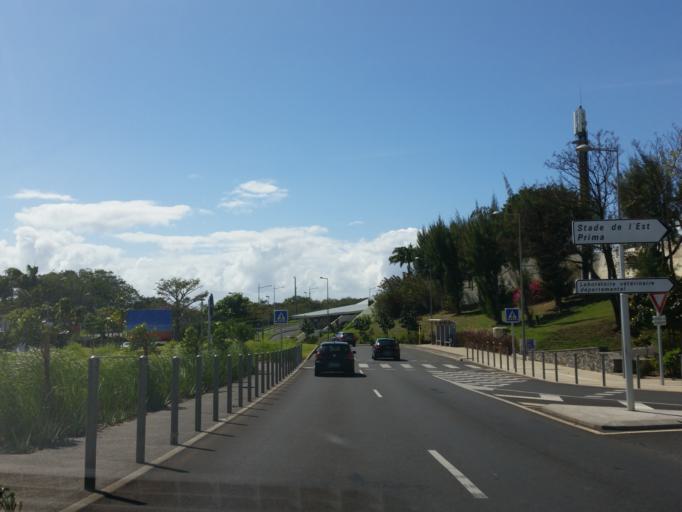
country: RE
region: Reunion
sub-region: Reunion
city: Sainte-Marie
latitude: -20.8944
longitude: 55.4998
